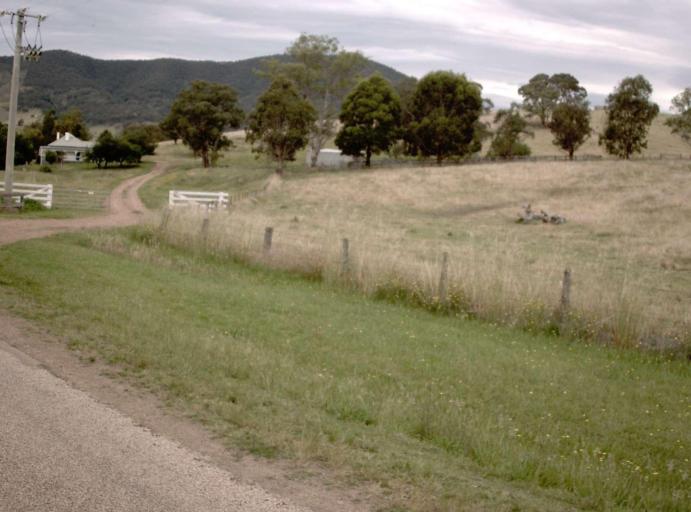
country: AU
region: Victoria
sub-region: East Gippsland
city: Bairnsdale
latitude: -37.4715
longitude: 147.2495
